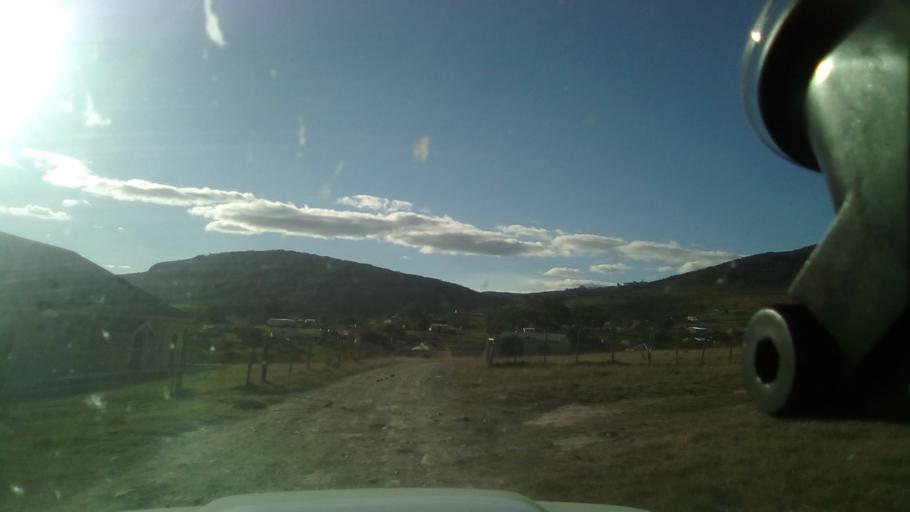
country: ZA
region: Eastern Cape
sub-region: Buffalo City Metropolitan Municipality
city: Bhisho
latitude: -32.7368
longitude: 27.3629
